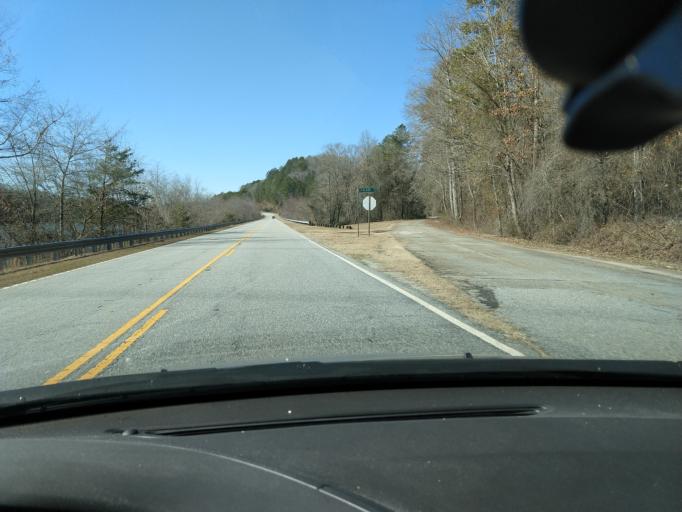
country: US
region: South Carolina
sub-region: Oconee County
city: Westminster
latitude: 34.6118
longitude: -83.2034
